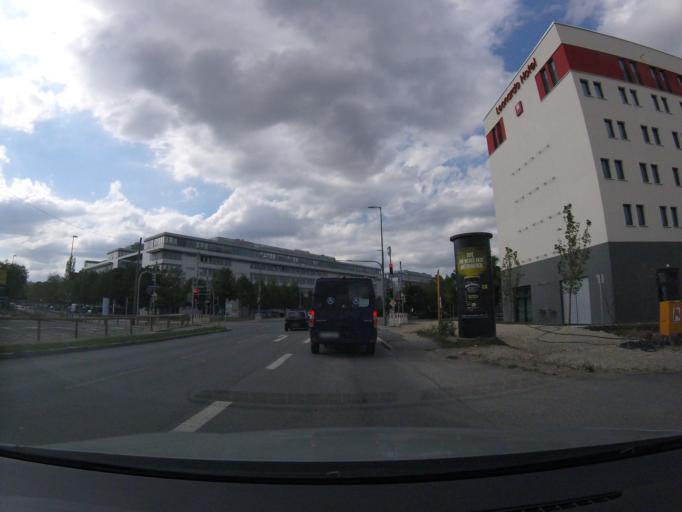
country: DE
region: Bavaria
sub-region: Upper Bavaria
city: Neubiberg
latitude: 48.0860
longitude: 11.6460
